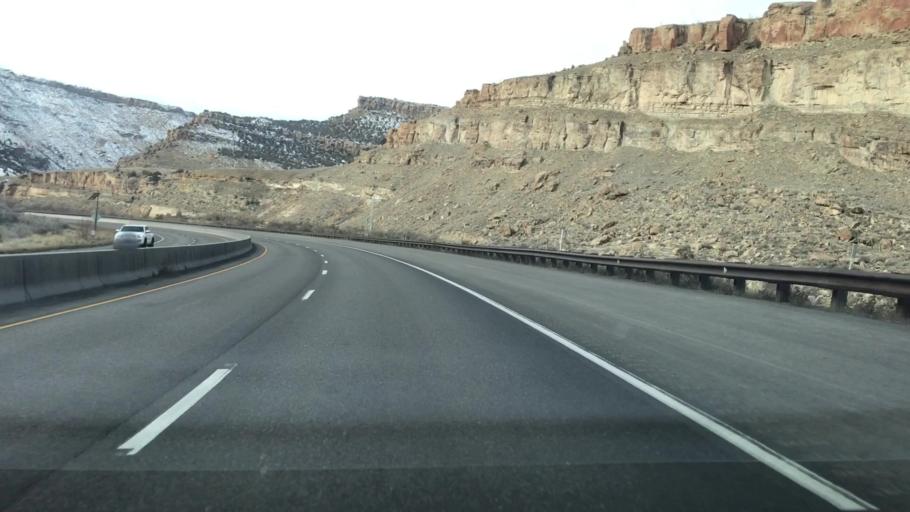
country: US
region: Colorado
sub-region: Mesa County
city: Palisade
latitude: 39.2389
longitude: -108.2652
